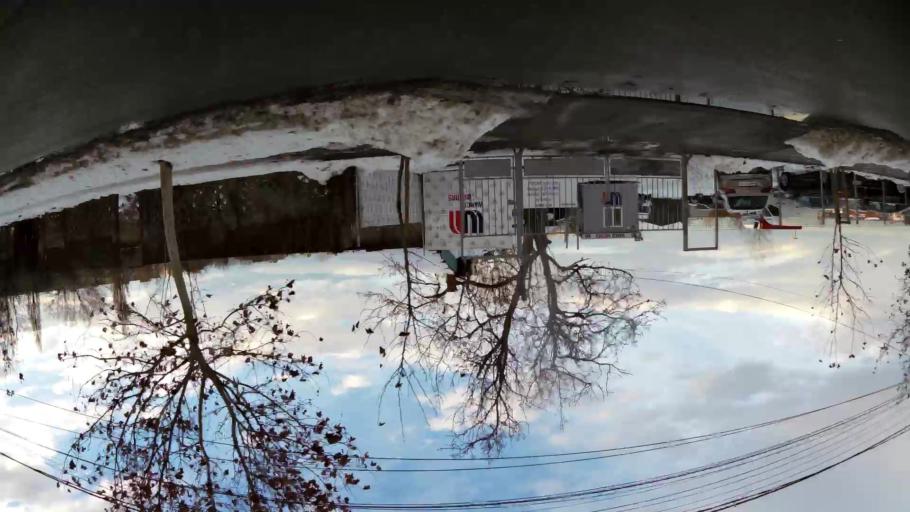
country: RO
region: Ilfov
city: Dobroesti
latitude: 44.4466
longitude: 26.1708
